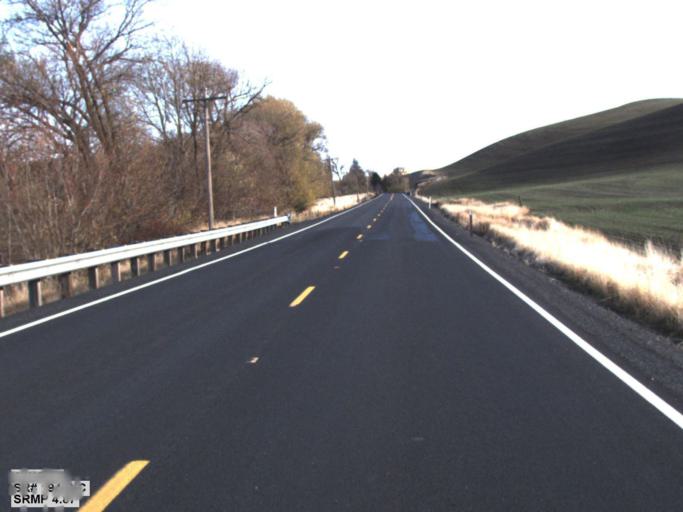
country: US
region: Washington
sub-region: Whitman County
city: Colfax
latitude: 46.7397
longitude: -117.4777
